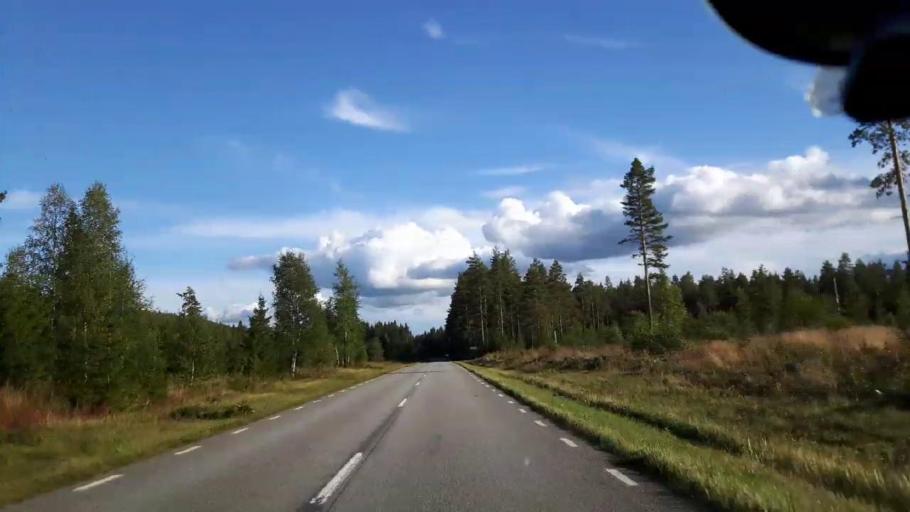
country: SE
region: Jaemtland
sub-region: Stroemsunds Kommun
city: Stroemsund
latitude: 63.4004
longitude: 15.5744
